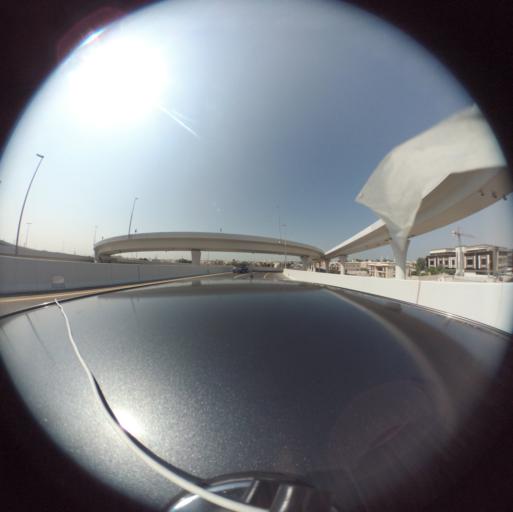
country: AE
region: Dubai
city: Dubai
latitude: 25.1647
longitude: 55.2346
